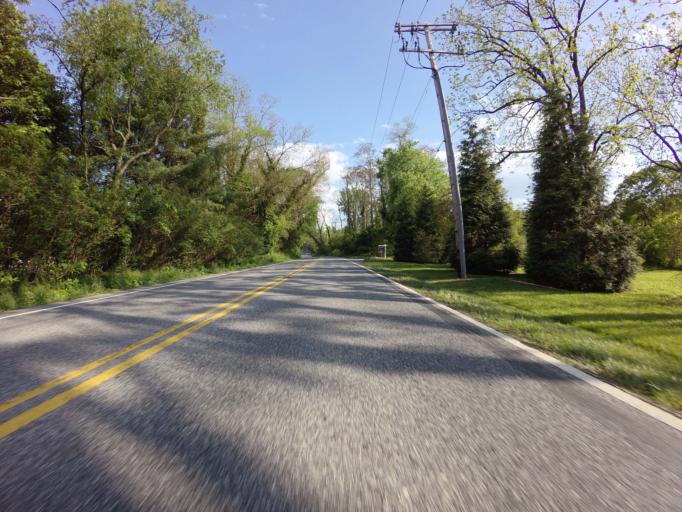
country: US
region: Maryland
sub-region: Baltimore County
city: Hunt Valley
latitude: 39.5111
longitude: -76.7145
